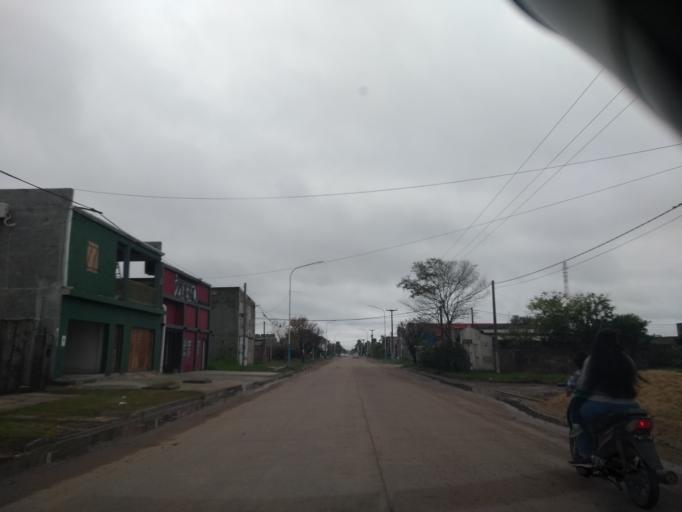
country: AR
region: Chaco
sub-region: Departamento de Quitilipi
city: Quitilipi
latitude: -26.8786
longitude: -60.2206
